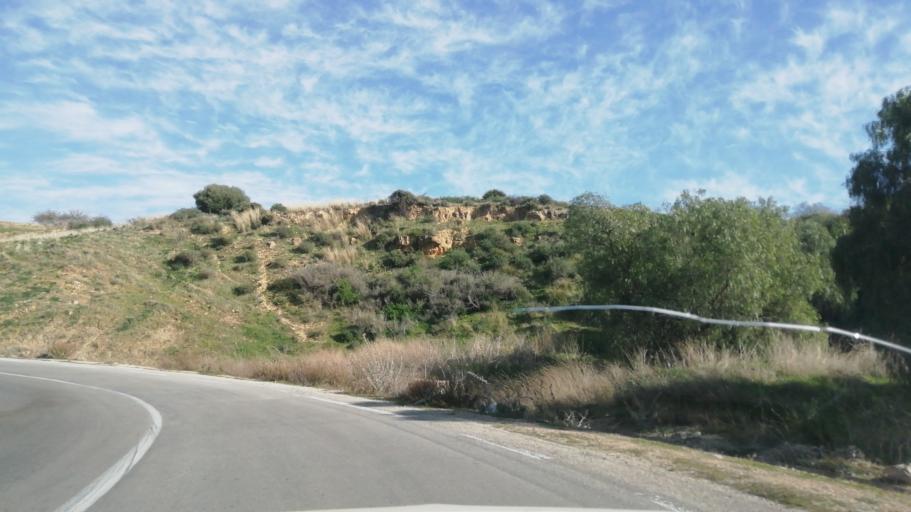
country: DZ
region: Tlemcen
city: Chetouane
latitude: 34.9607
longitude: -1.2462
